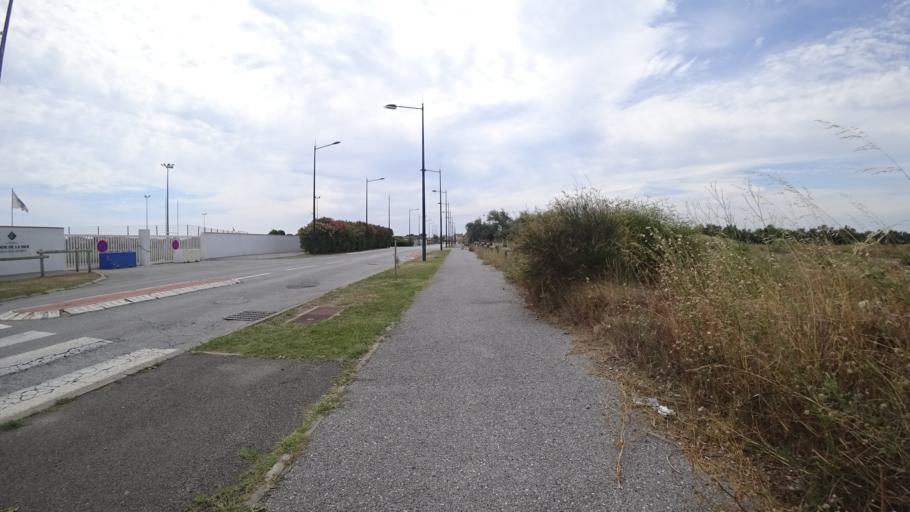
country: FR
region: Languedoc-Roussillon
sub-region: Departement des Pyrenees-Orientales
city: Le Barcares
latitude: 42.7978
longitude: 3.0293
